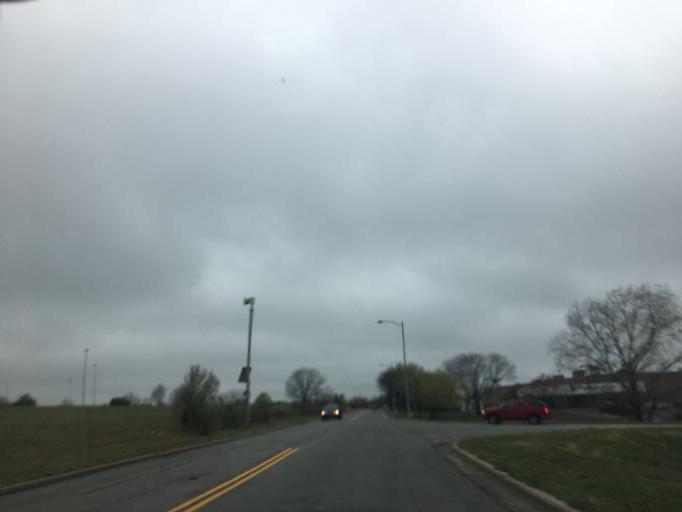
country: US
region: Kansas
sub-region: Johnson County
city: Lenexa
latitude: 38.9816
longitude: -94.7100
